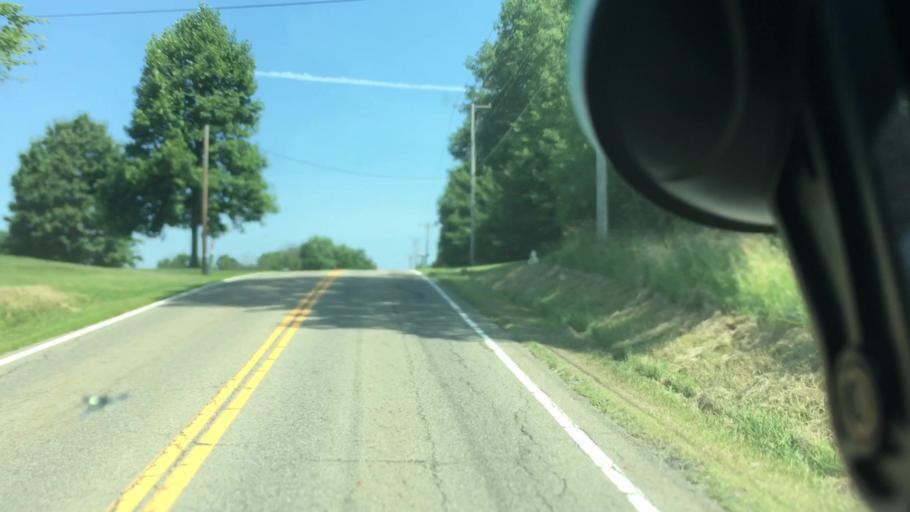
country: US
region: Ohio
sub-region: Columbiana County
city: Salem
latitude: 40.8462
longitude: -80.8576
